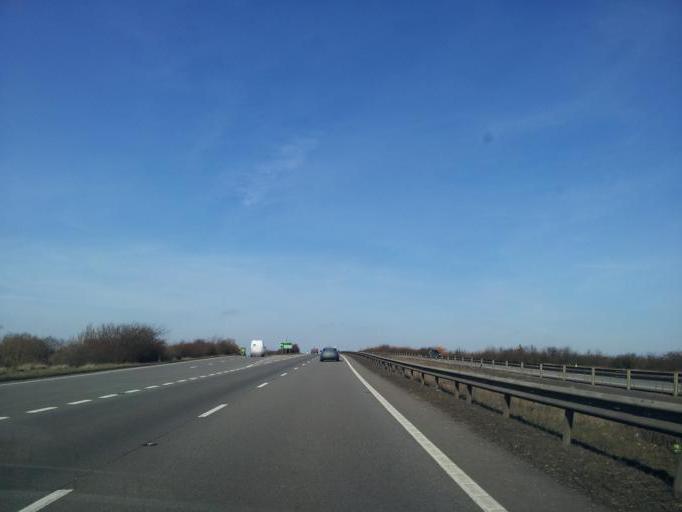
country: GB
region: England
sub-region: Cambridgeshire
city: Brampton
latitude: 52.3282
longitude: -0.2476
